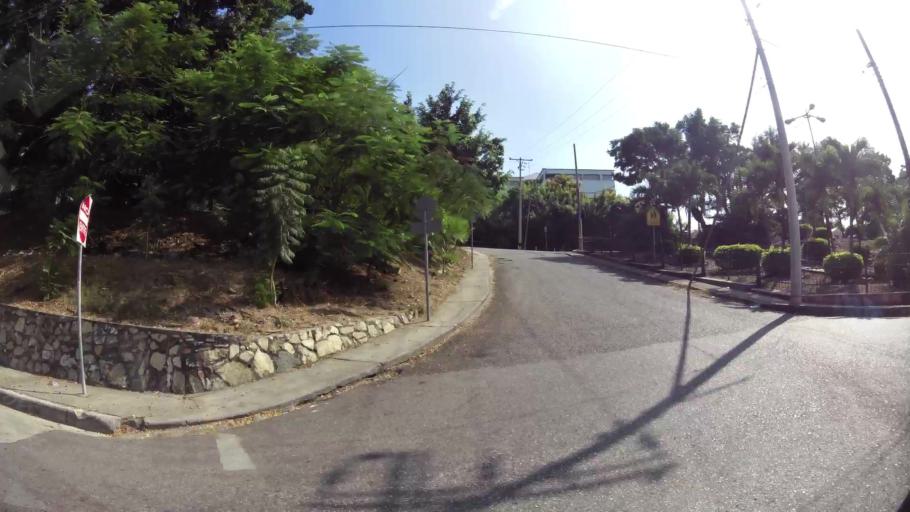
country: EC
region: Guayas
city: Guayaquil
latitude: -2.1626
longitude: -79.9372
